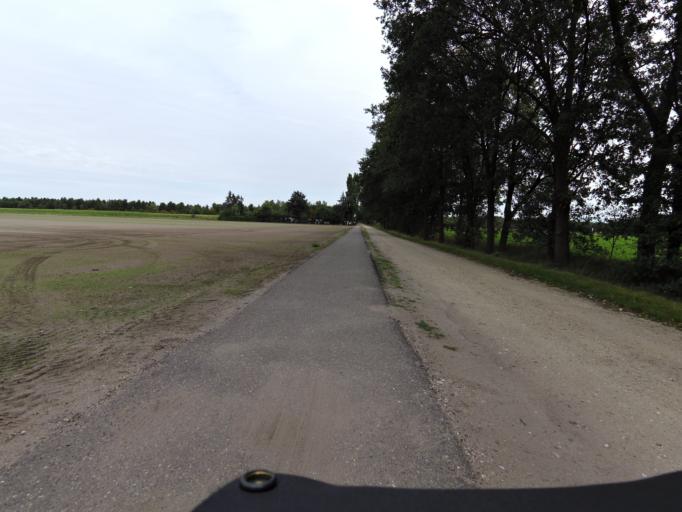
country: NL
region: Limburg
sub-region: Gemeente Bergen
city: Wellerlooi
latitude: 51.5787
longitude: 6.1141
